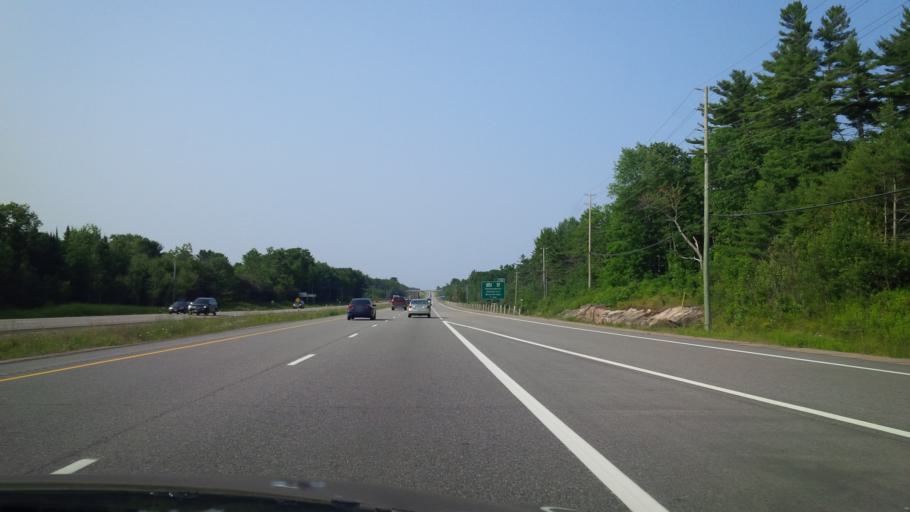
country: CA
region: Ontario
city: Bracebridge
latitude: 45.0082
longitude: -79.2991
